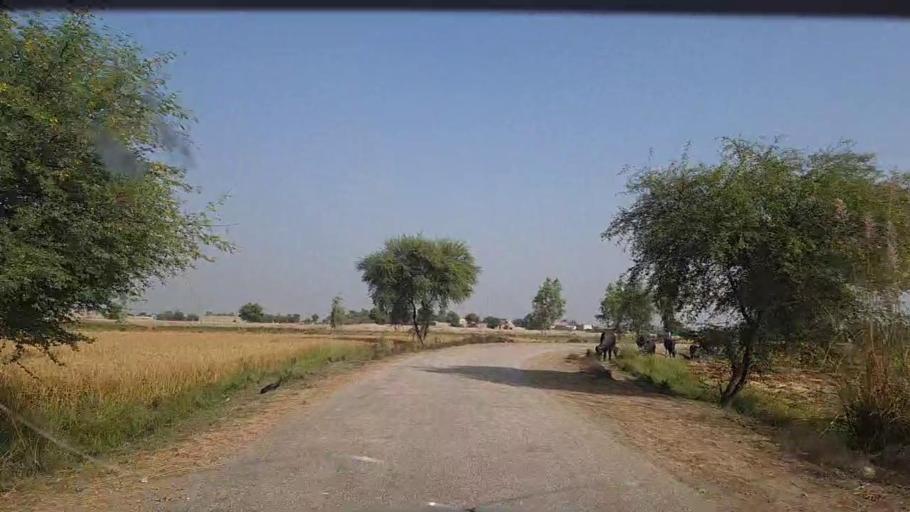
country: PK
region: Sindh
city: Shikarpur
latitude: 28.1169
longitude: 68.5752
